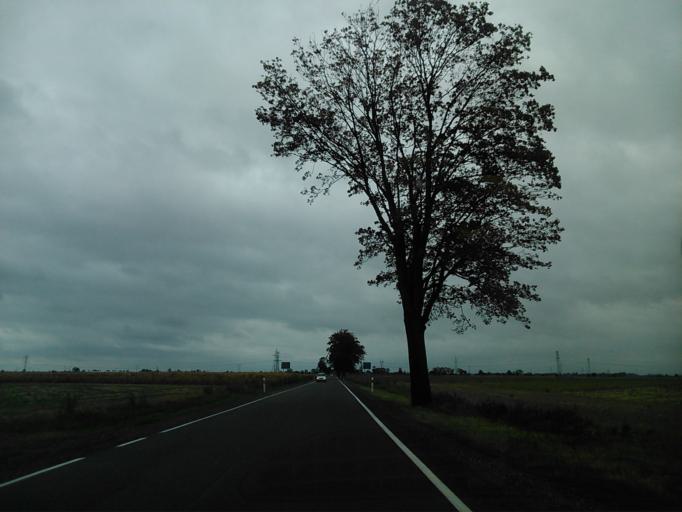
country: PL
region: Kujawsko-Pomorskie
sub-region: Powiat inowroclawski
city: Kruszwica
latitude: 52.6718
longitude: 18.2538
